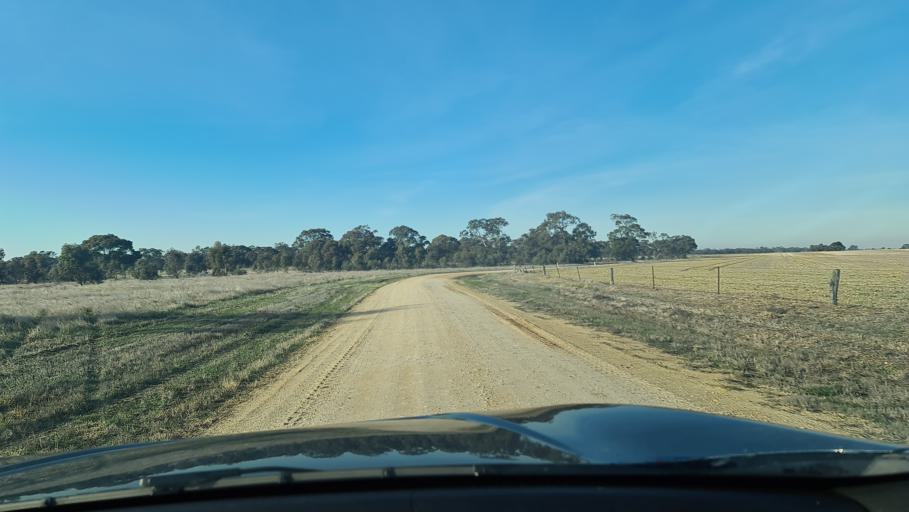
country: AU
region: Victoria
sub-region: Horsham
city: Horsham
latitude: -36.3562
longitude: 142.3959
